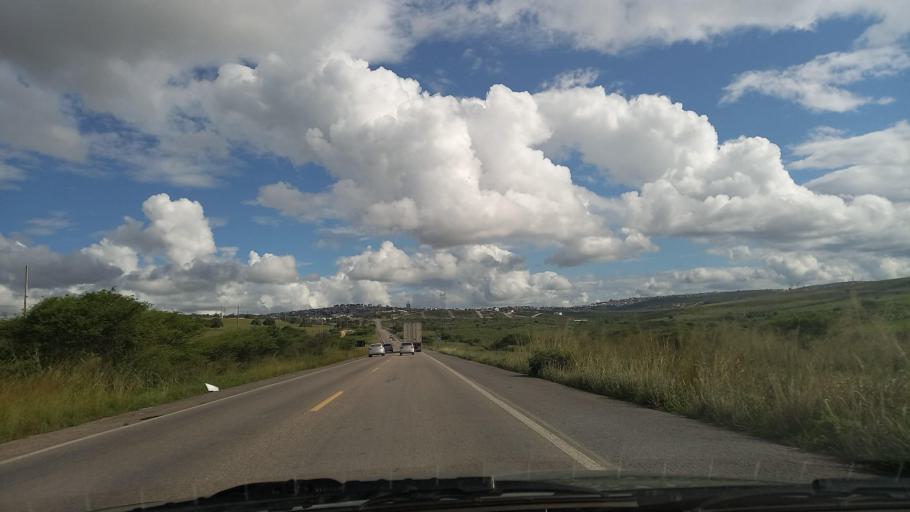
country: BR
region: Pernambuco
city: Garanhuns
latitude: -8.8435
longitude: -36.4587
